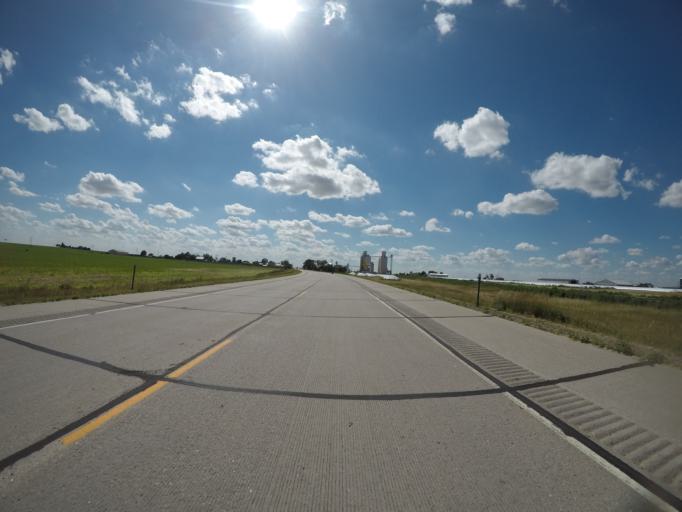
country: US
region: Colorado
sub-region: Phillips County
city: Holyoke
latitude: 40.6116
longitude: -102.4657
